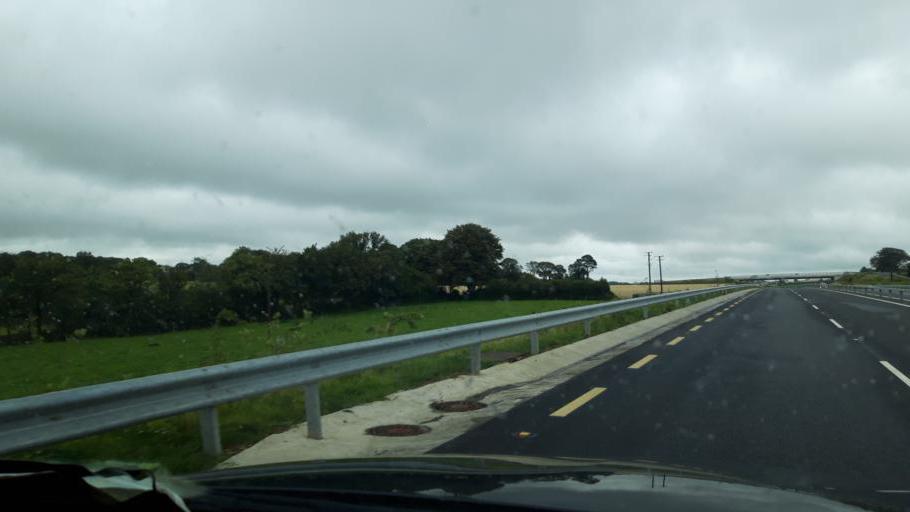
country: IE
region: Leinster
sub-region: Loch Garman
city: New Ross
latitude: 52.3729
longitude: -6.9261
